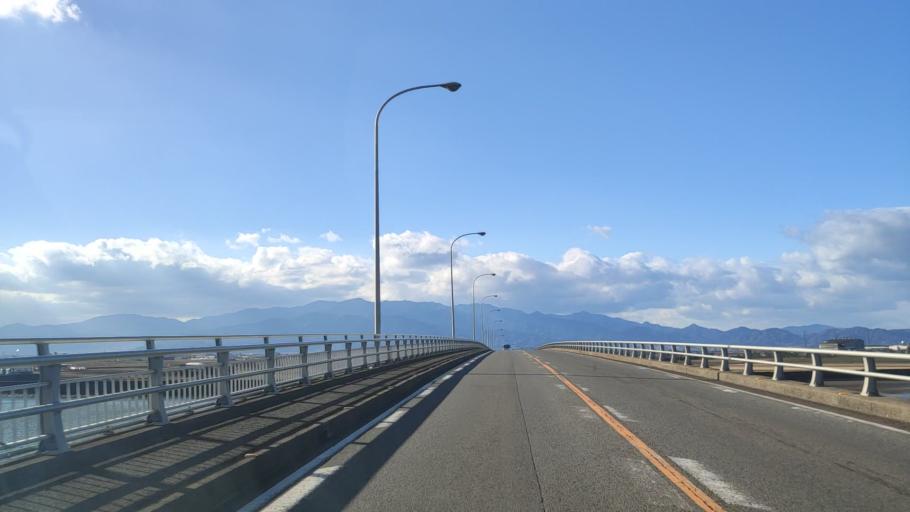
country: JP
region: Ehime
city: Saijo
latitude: 33.9156
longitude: 133.1346
